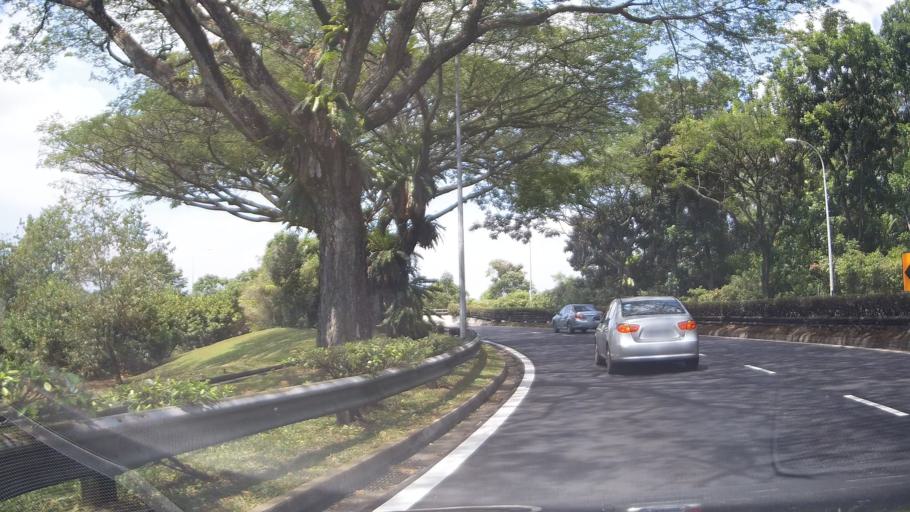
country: SG
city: Singapore
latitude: 1.3339
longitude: 103.7652
